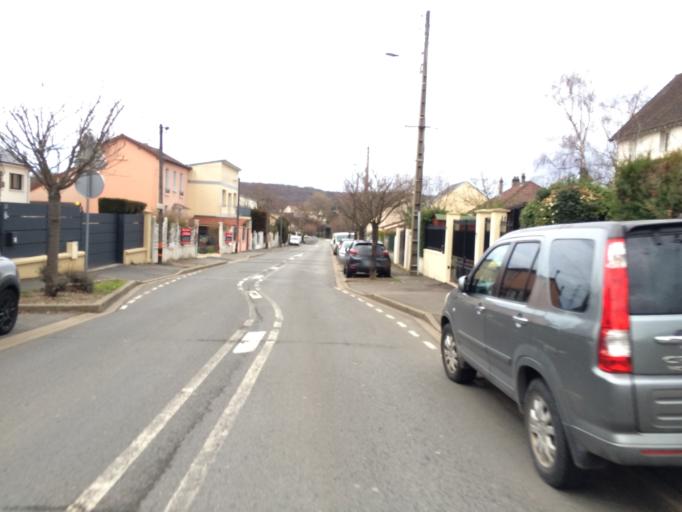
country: FR
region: Ile-de-France
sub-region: Departement de l'Essonne
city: Igny
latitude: 48.7341
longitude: 2.2263
